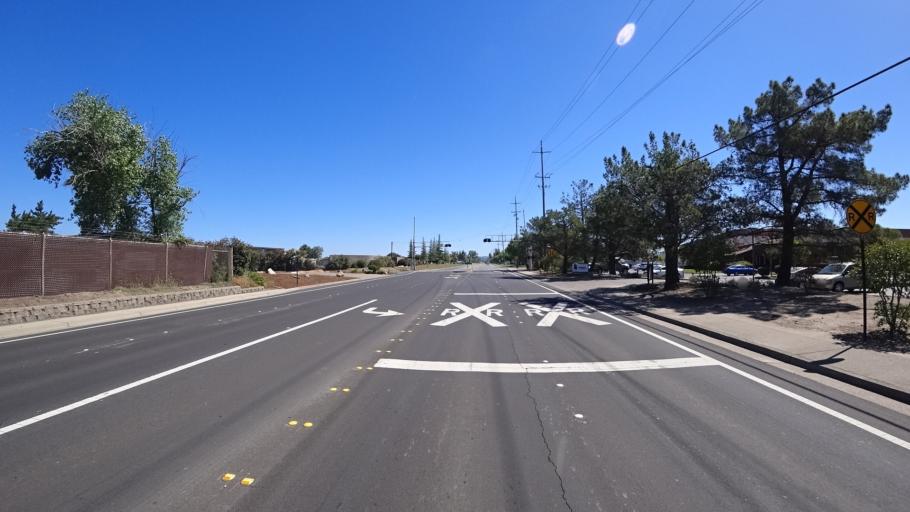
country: US
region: California
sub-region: Placer County
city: Rocklin
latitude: 38.8011
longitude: -121.2239
